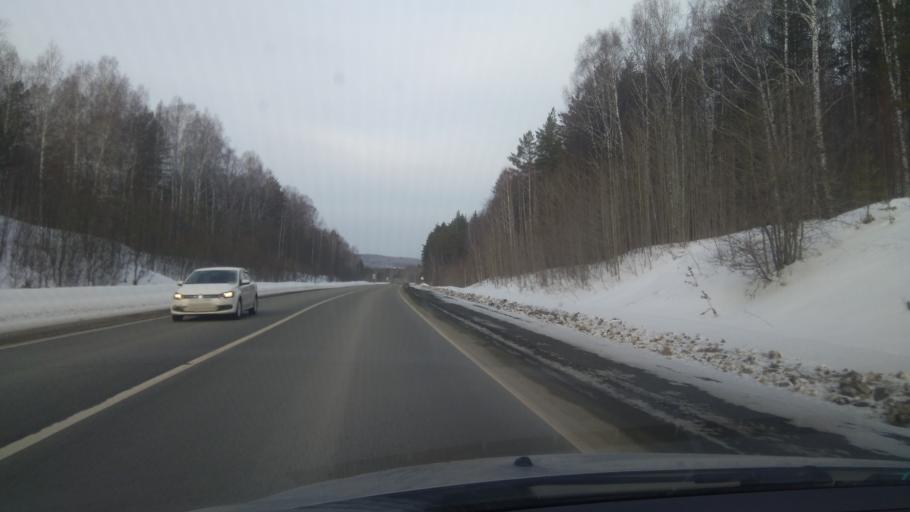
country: RU
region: Sverdlovsk
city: Bisert'
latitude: 56.8353
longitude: 58.8859
